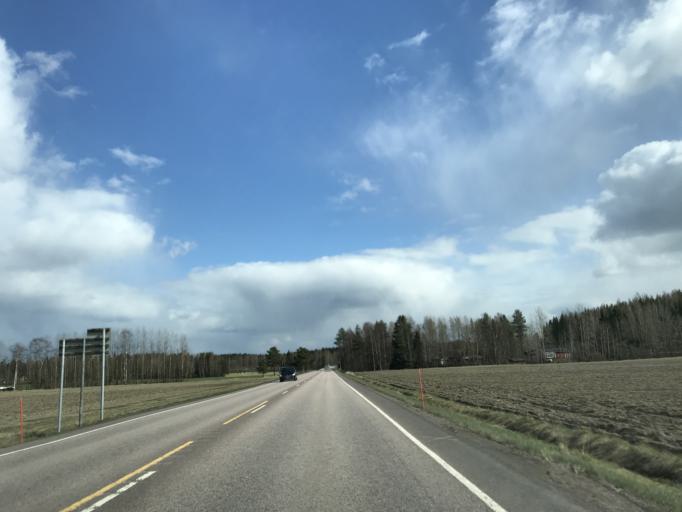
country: FI
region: Uusimaa
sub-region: Helsinki
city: Hyvinge
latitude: 60.5384
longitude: 24.9011
